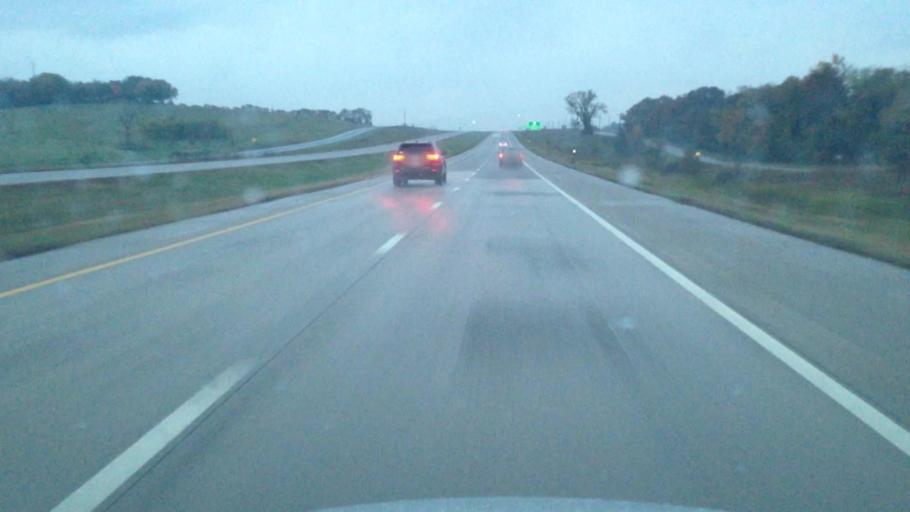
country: US
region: Kansas
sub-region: Douglas County
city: Baldwin City
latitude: 38.7998
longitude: -95.2692
